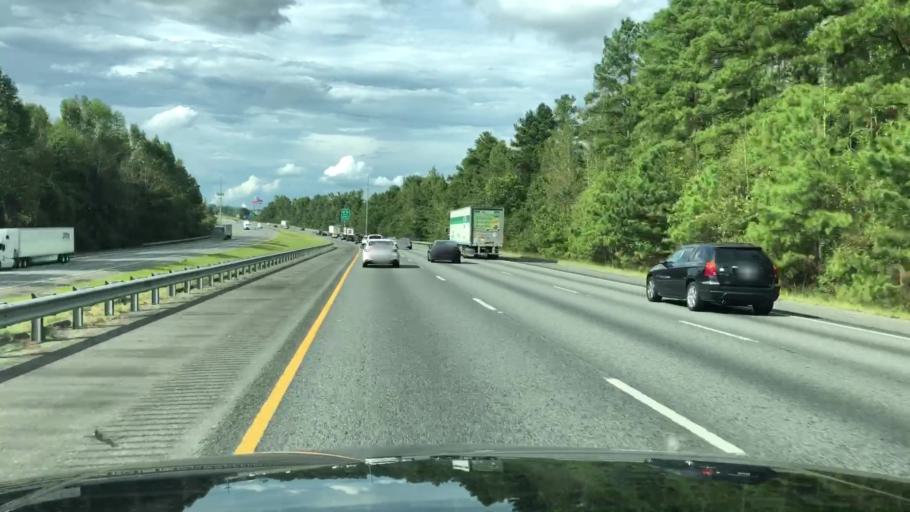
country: US
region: Georgia
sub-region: Bibb County
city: West Point
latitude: 32.7970
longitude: -83.7199
